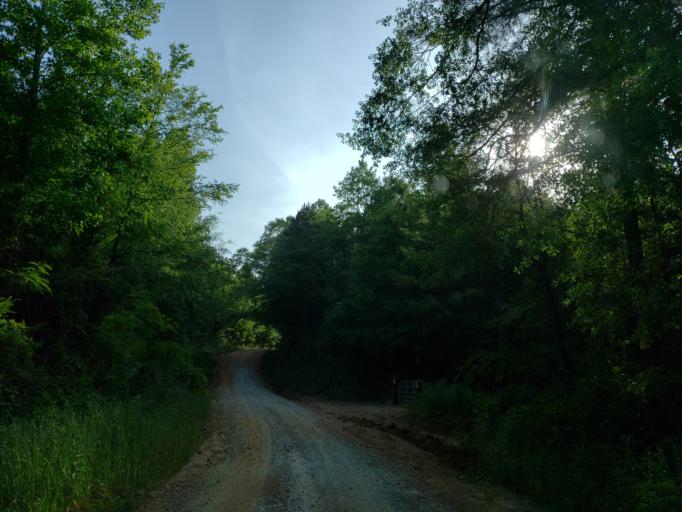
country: US
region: Georgia
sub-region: Carroll County
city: Bowdon
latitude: 33.4764
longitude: -85.3081
